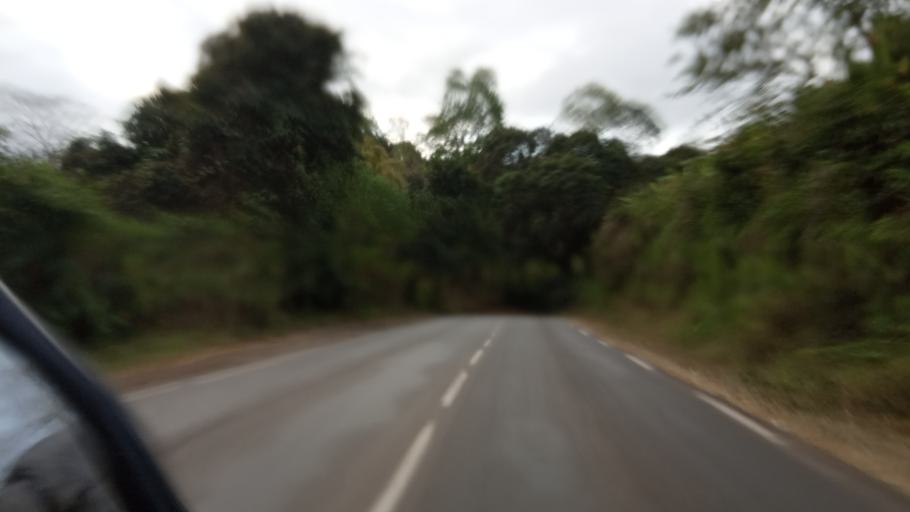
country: YT
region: Dembeni
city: Dembeni
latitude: -12.8365
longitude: 45.1799
